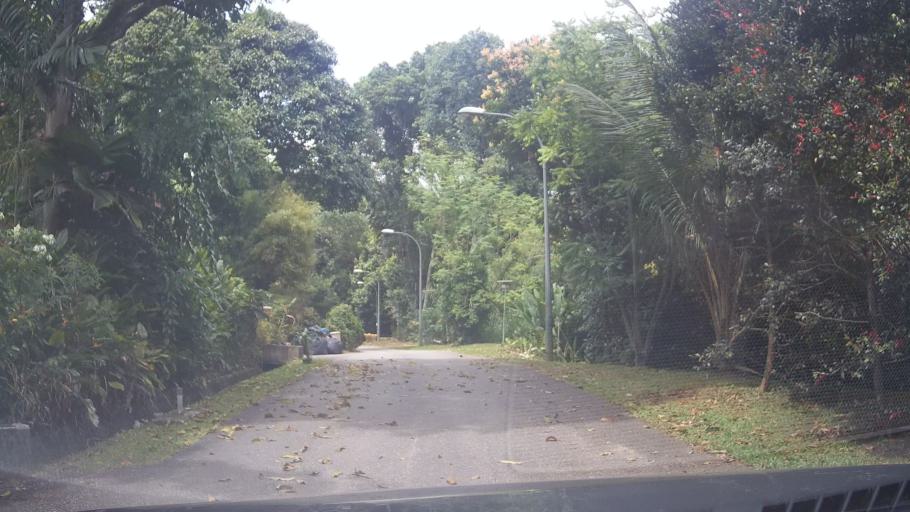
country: MY
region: Johor
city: Johor Bahru
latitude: 1.4528
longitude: 103.7892
